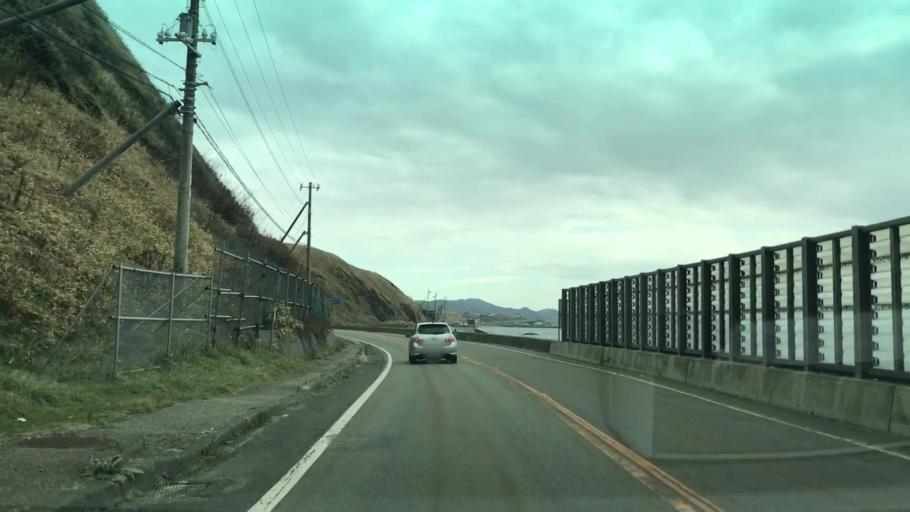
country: JP
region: Hokkaido
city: Shizunai-furukawacho
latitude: 42.0536
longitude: 143.0860
